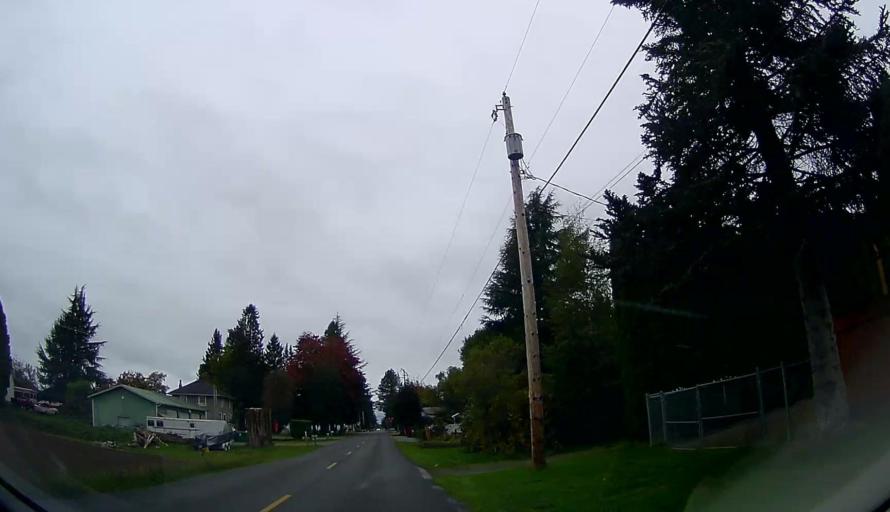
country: US
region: Washington
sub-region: Skagit County
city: Sedro-Woolley
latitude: 48.5033
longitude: -122.2110
